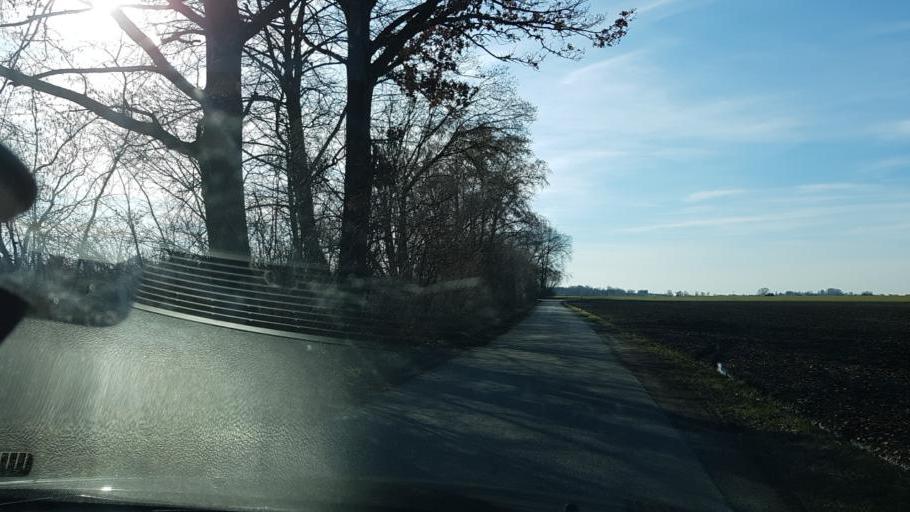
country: DE
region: Bavaria
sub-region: Upper Bavaria
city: Oberschweinbach
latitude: 48.2190
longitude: 11.1615
